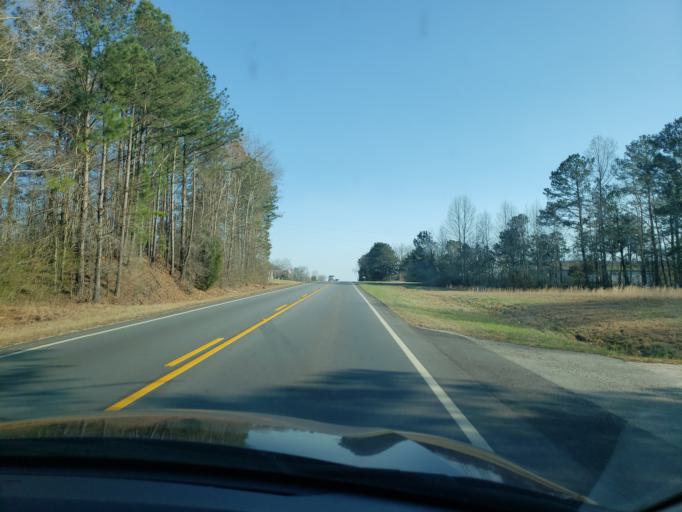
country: US
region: Alabama
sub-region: Randolph County
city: Wedowee
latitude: 33.2790
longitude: -85.4673
